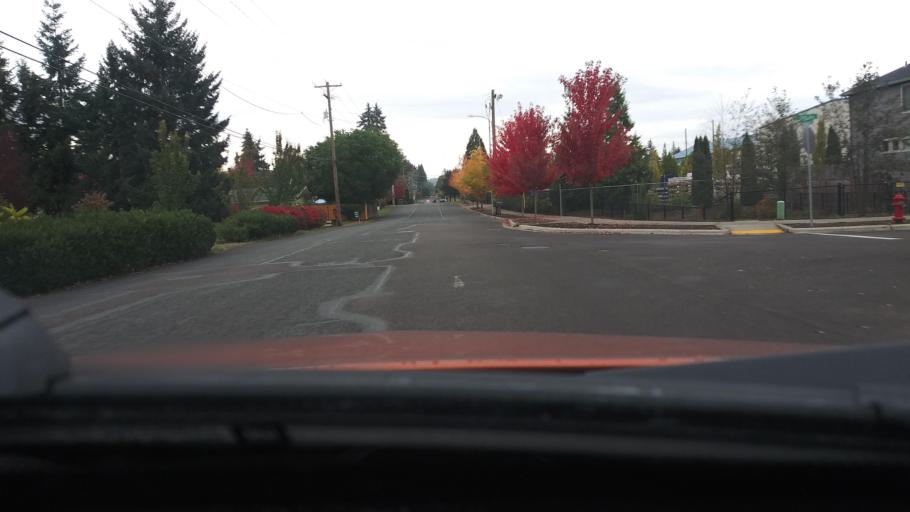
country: US
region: Oregon
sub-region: Washington County
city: Forest Grove
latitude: 45.5264
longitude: -123.0991
